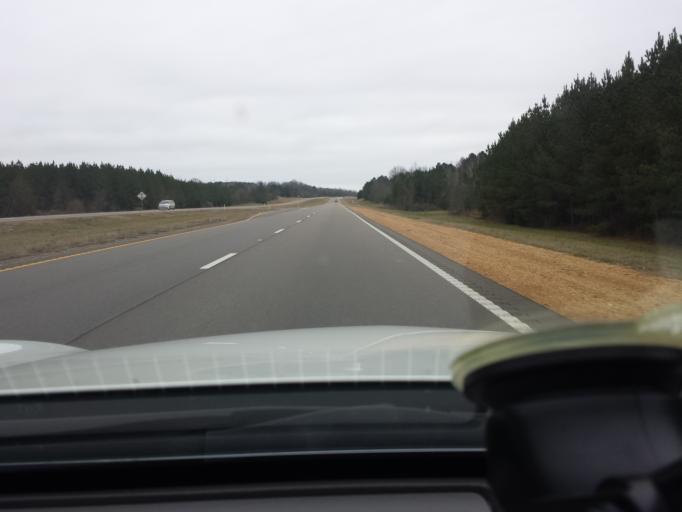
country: US
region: Mississippi
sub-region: Lee County
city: Shannon
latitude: 34.0957
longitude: -88.7005
